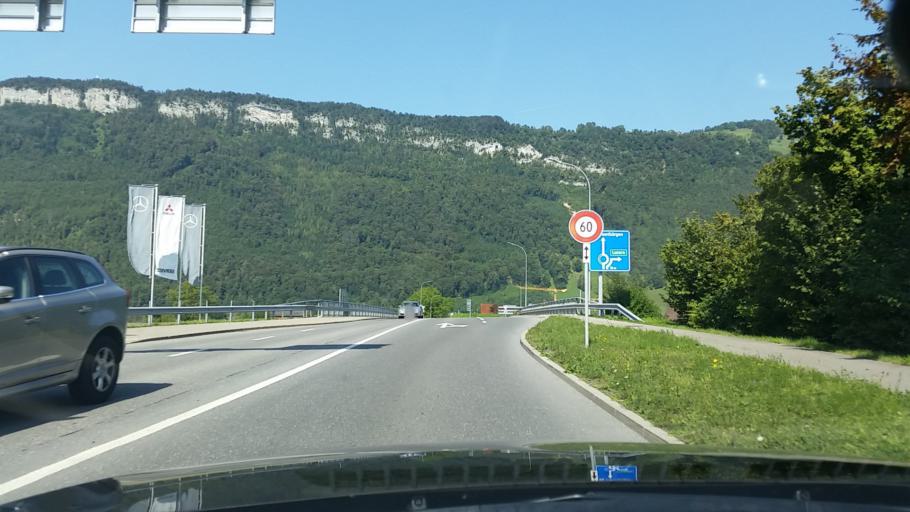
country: CH
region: Nidwalden
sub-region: Nidwalden
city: Stans
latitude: 46.9652
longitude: 8.3847
